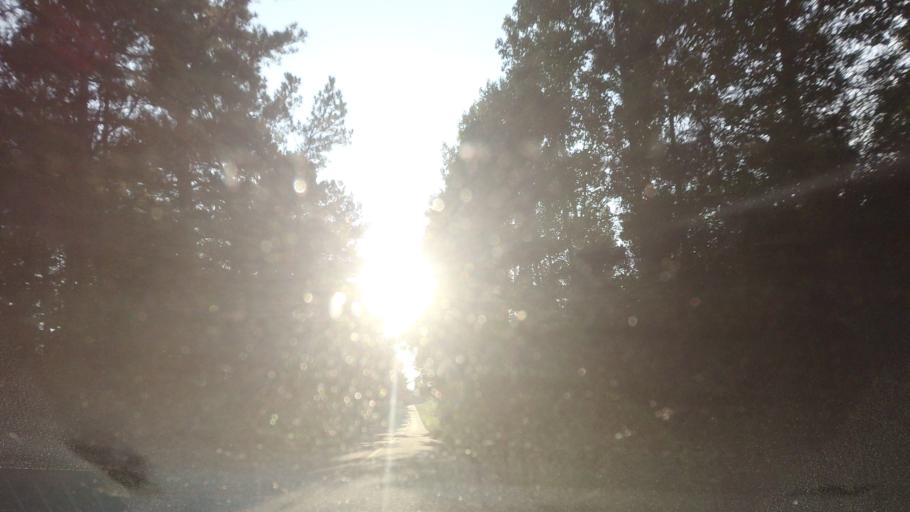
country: US
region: Georgia
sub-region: Bibb County
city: West Point
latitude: 32.9405
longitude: -83.7704
